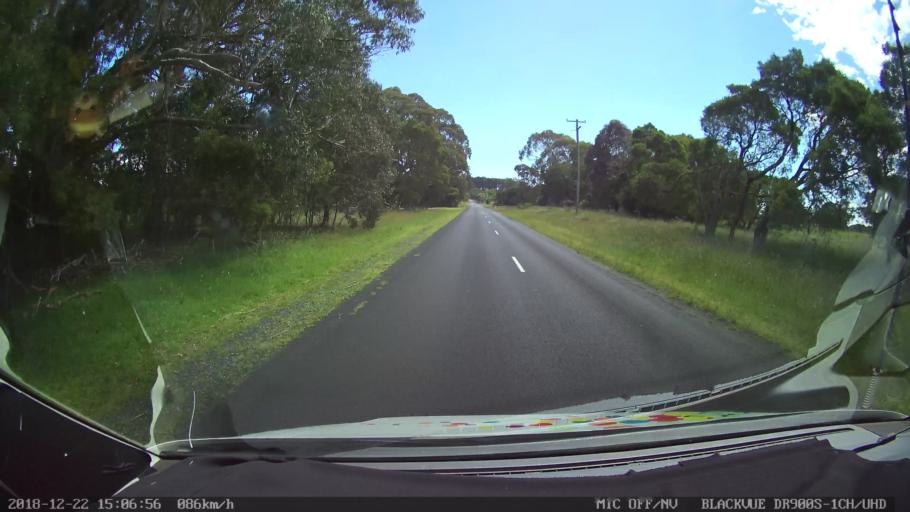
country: AU
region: New South Wales
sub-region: Bellingen
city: Dorrigo
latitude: -30.2966
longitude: 152.4211
